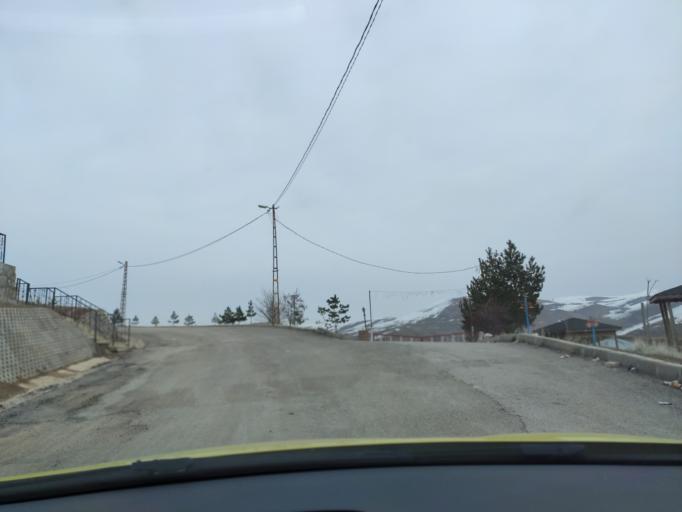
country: TR
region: Bayburt
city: Bayburt
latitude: 40.2605
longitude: 40.2205
